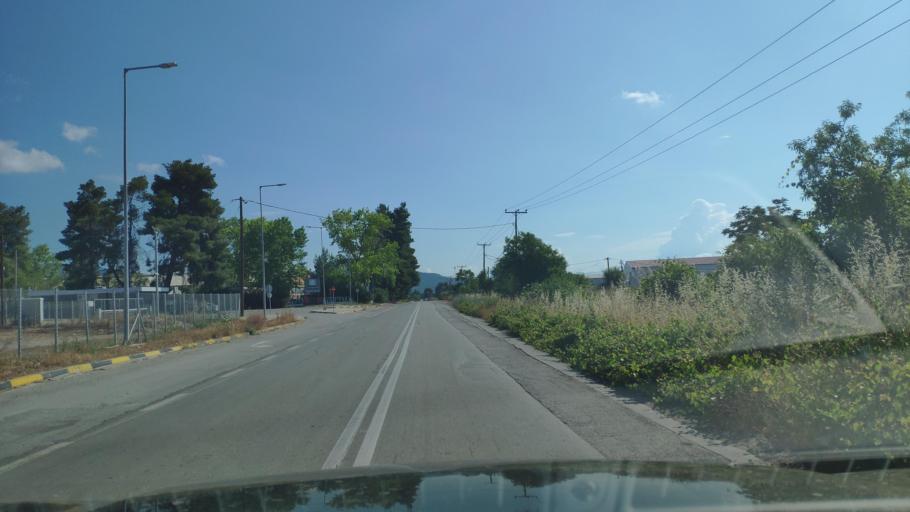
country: GR
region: Central Greece
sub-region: Nomos Voiotias
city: Arma
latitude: 38.3827
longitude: 23.4971
